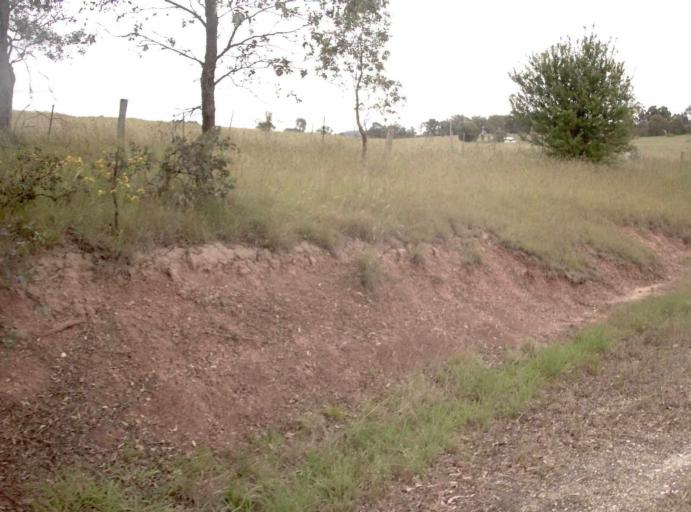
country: AU
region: Victoria
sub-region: East Gippsland
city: Bairnsdale
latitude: -37.7629
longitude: 147.3216
